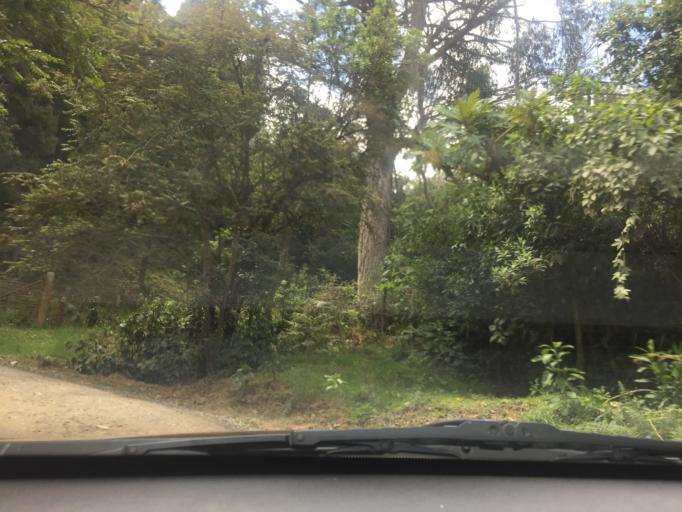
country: CO
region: Cundinamarca
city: Zipacon
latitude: 4.7864
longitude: -74.3745
